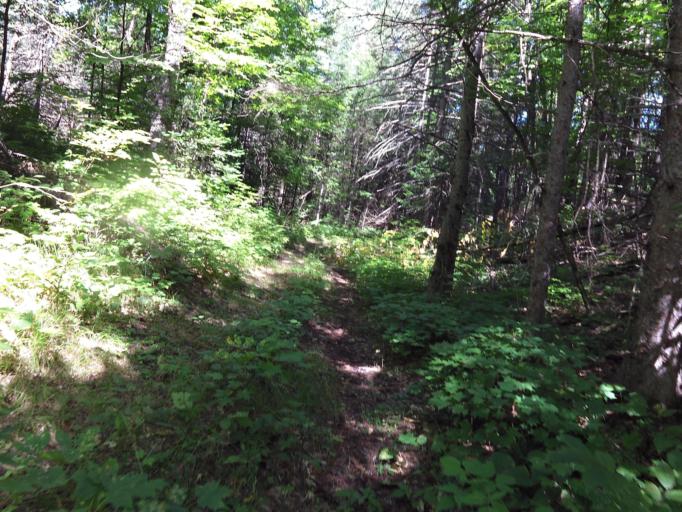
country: CA
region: Ontario
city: Renfrew
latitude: 45.0261
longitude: -76.6960
